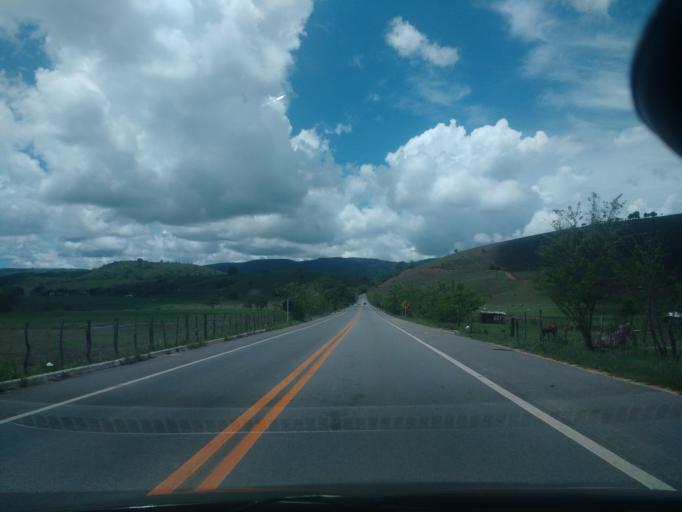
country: BR
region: Alagoas
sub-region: Uniao Dos Palmares
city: Uniao dos Palmares
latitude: -9.1343
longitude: -36.0248
